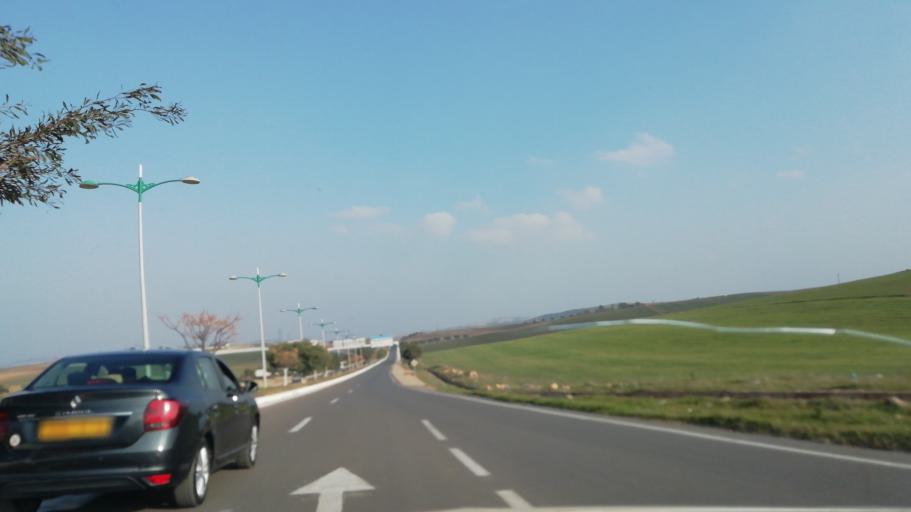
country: DZ
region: Ain Temouchent
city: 'Ain Temouchent
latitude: 35.2925
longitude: -1.1196
